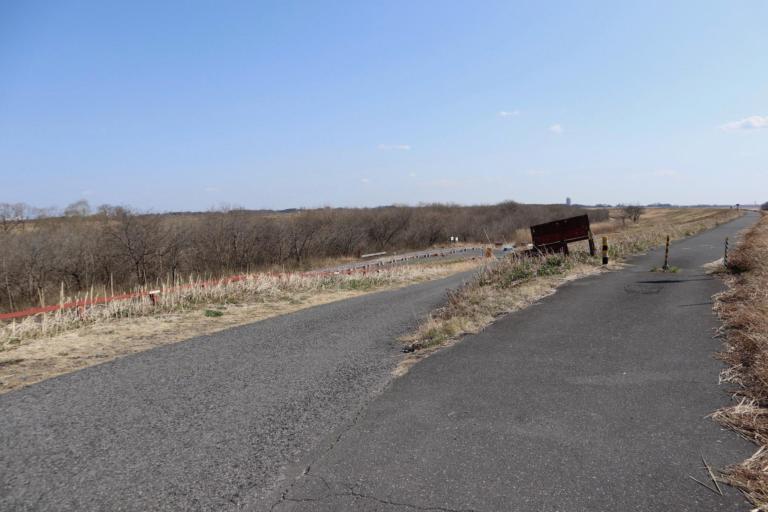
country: JP
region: Tochigi
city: Fujioka
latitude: 36.2351
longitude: 139.6840
